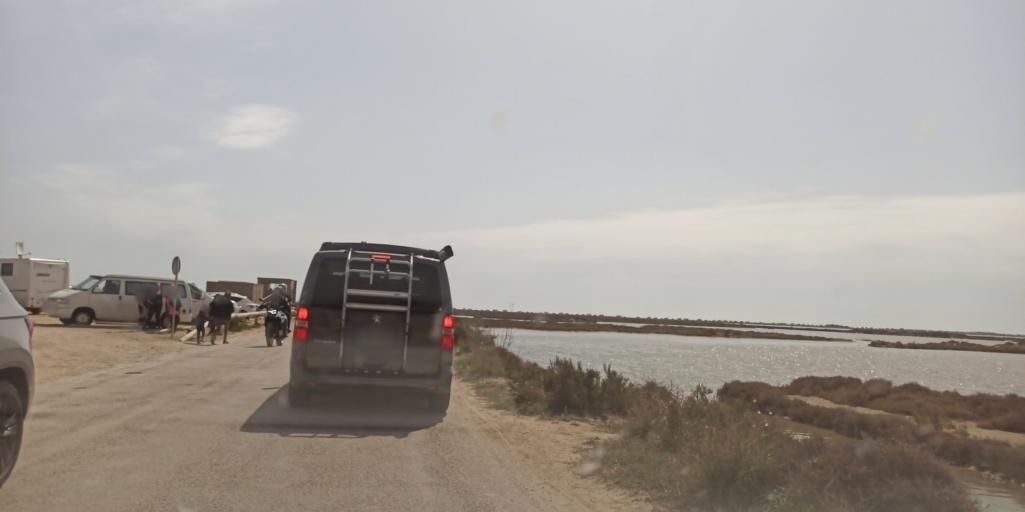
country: ES
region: Catalonia
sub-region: Provincia de Tarragona
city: Deltebre
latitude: 40.6409
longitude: 0.7392
